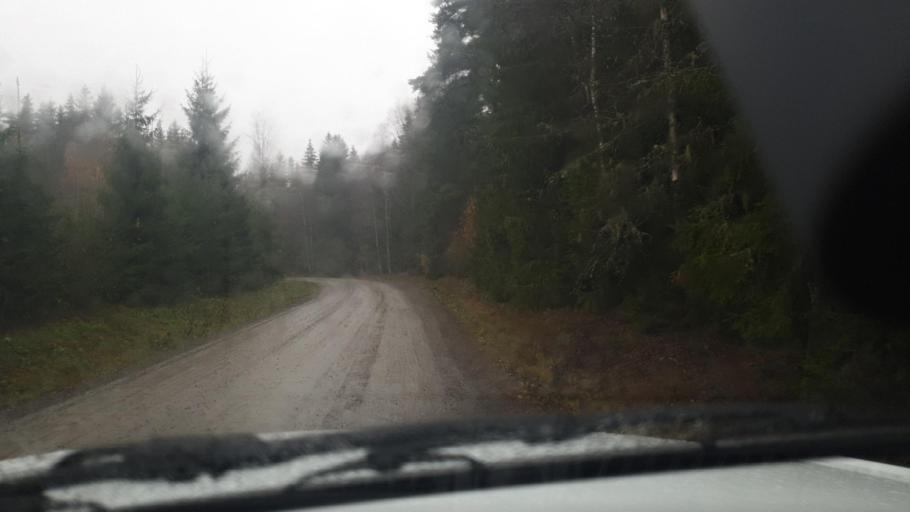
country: SE
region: Vaermland
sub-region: Sunne Kommun
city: Sunne
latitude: 59.8068
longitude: 13.0782
